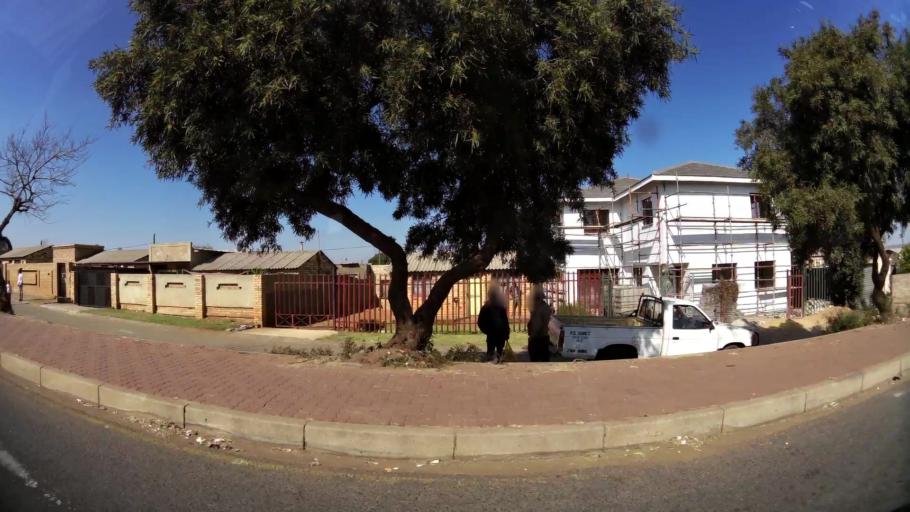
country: ZA
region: Gauteng
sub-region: City of Johannesburg Metropolitan Municipality
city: Soweto
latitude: -26.2837
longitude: 27.8557
